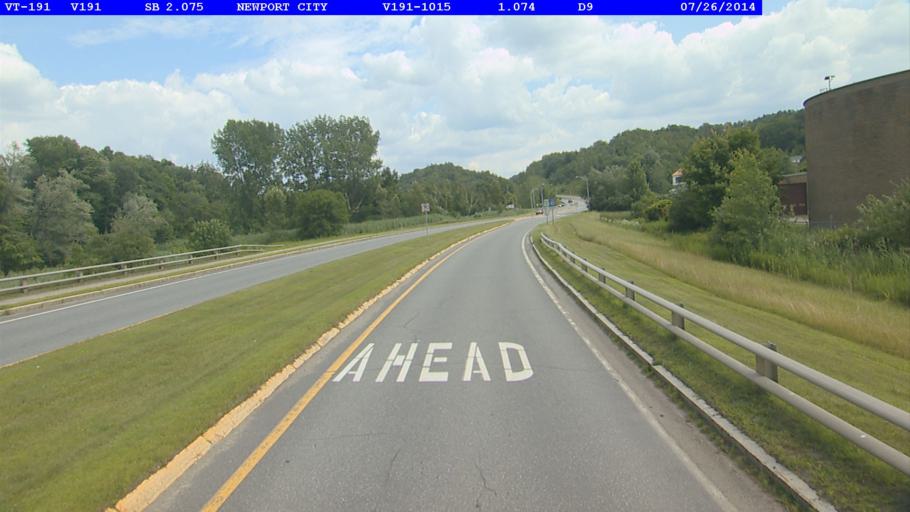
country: US
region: Vermont
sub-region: Orleans County
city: Newport
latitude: 44.9408
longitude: -72.2000
